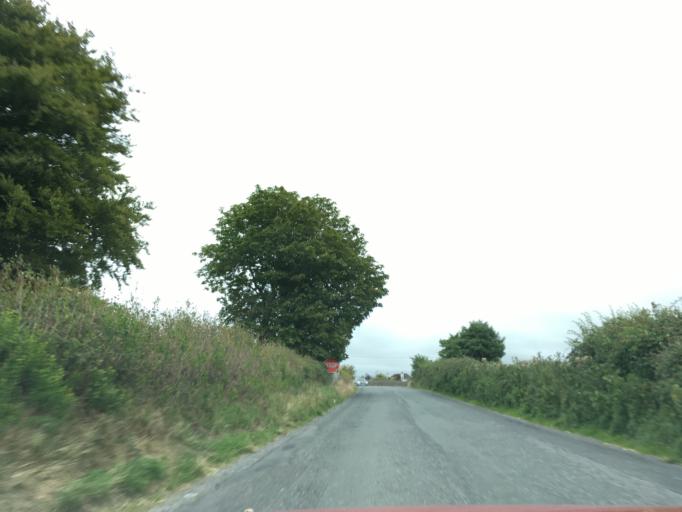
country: IE
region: Munster
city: Cashel
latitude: 52.4773
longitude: -7.8933
